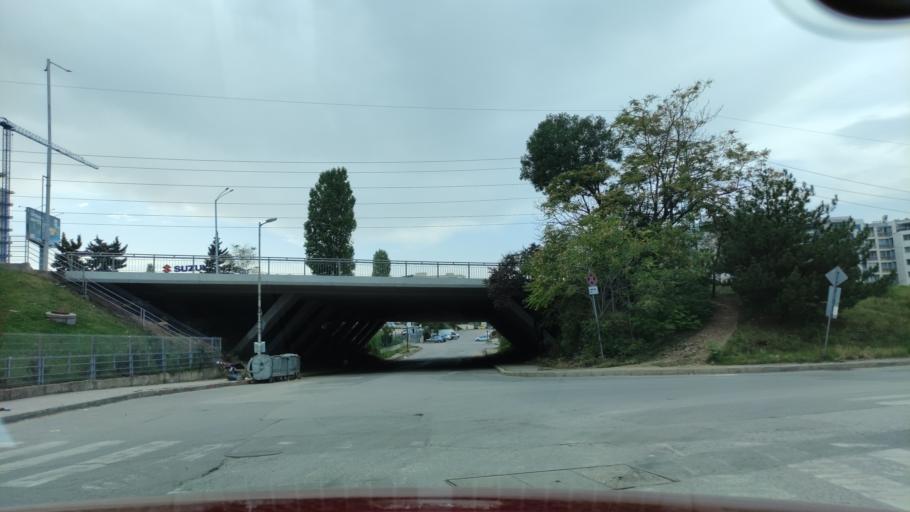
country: BG
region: Sofia-Capital
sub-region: Stolichna Obshtina
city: Sofia
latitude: 42.6566
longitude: 23.2855
